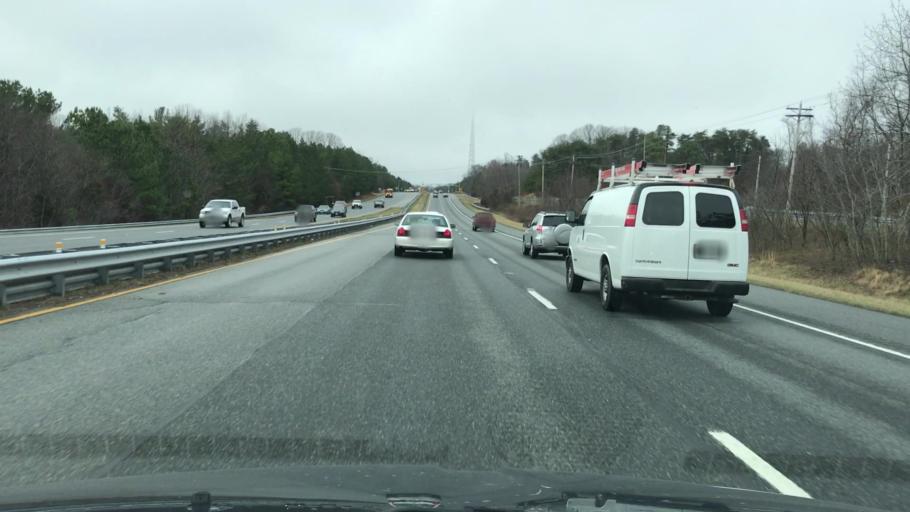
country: US
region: Maryland
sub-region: Calvert County
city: Lusby
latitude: 38.4292
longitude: -76.4644
